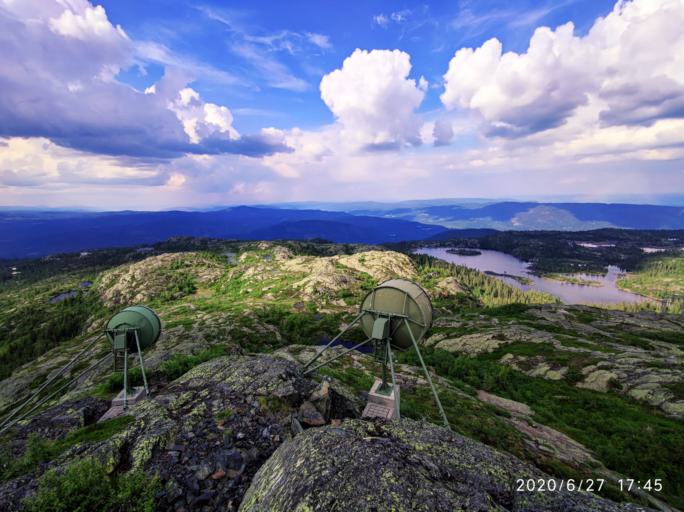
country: NO
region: Buskerud
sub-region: Kongsberg
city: Kongsberg
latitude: 59.6717
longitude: 9.5217
